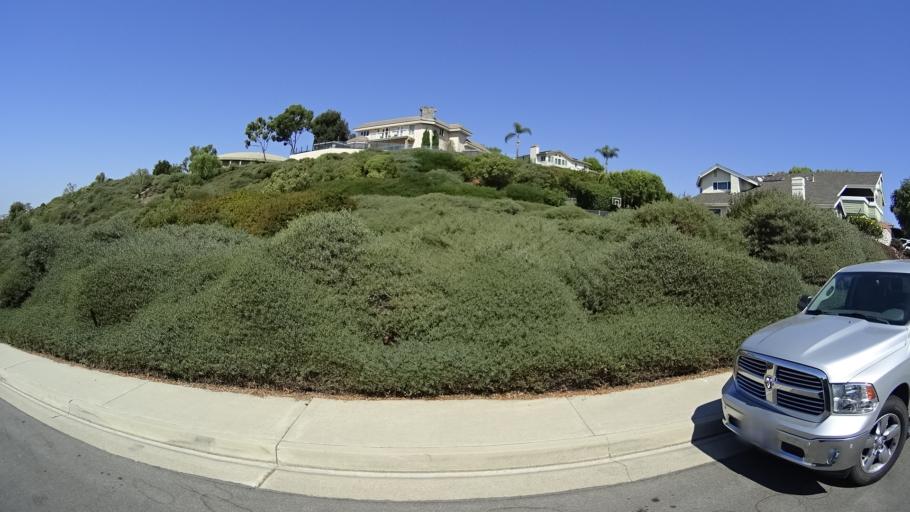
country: US
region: California
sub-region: Orange County
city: San Clemente
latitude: 33.4539
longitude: -117.6348
